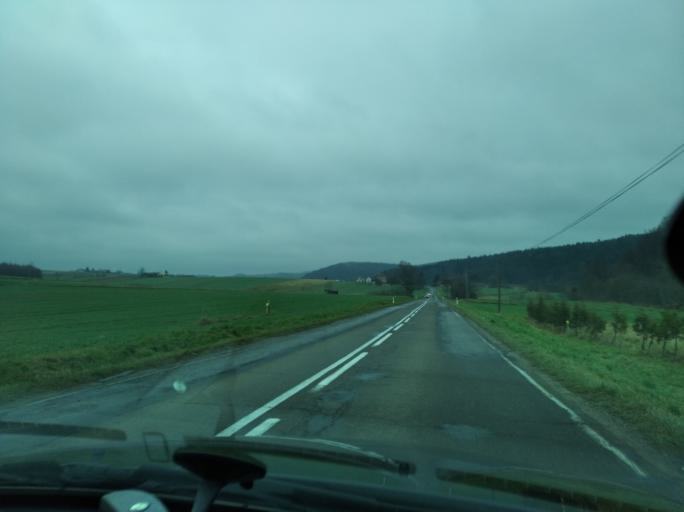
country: PL
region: Subcarpathian Voivodeship
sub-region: Powiat rzeszowski
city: Dynow
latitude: 49.8514
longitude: 22.2471
